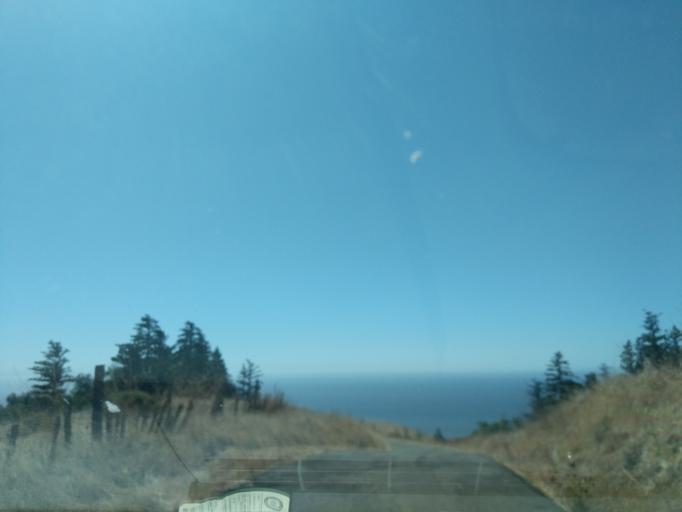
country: US
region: California
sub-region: Sonoma County
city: Monte Rio
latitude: 38.5336
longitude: -123.2228
